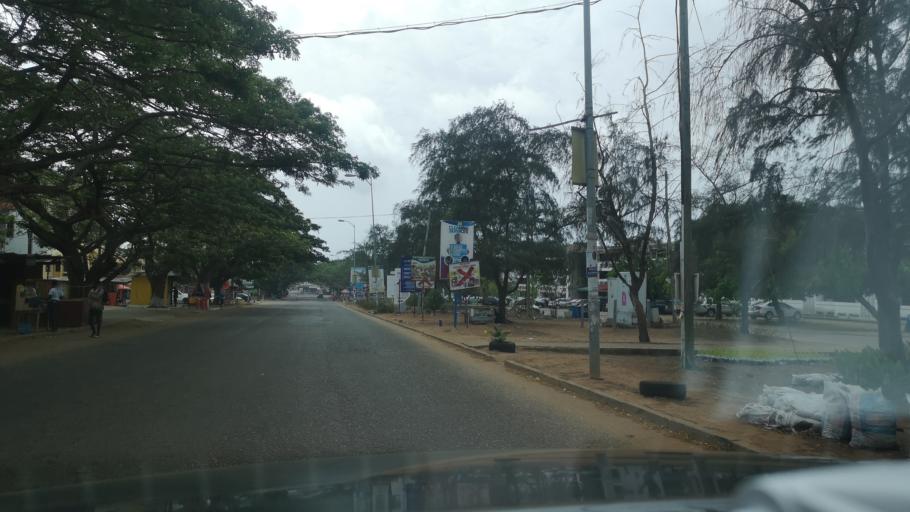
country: GH
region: Greater Accra
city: Nungua
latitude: 5.6224
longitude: -0.0638
